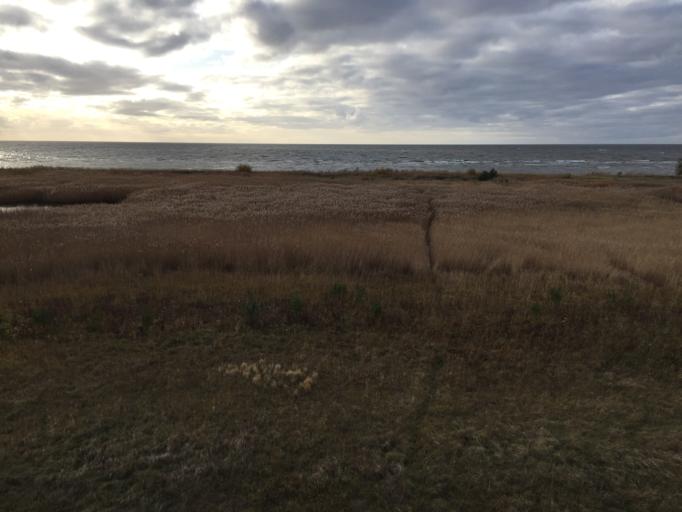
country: LV
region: Salacgrivas
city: Ainazi
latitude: 57.8255
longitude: 24.3363
